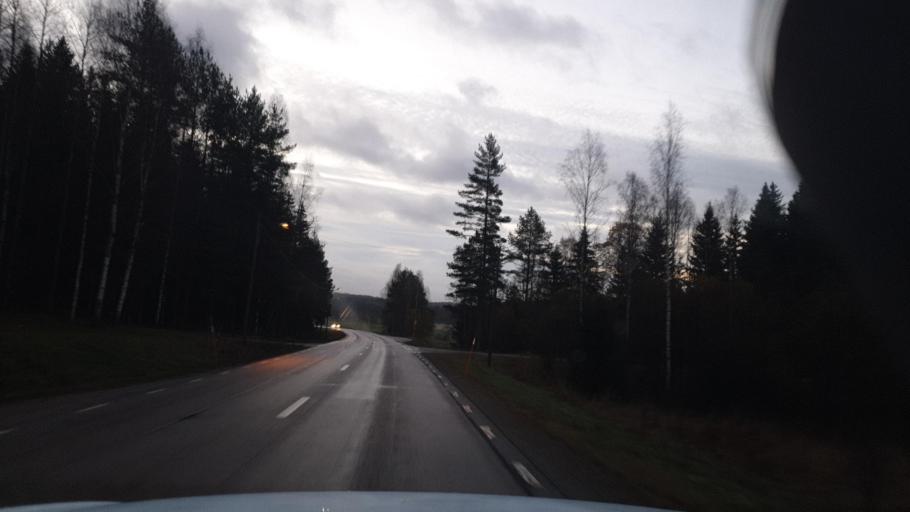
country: SE
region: Vaermland
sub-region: Arvika Kommun
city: Arvika
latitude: 59.6403
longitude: 12.7860
